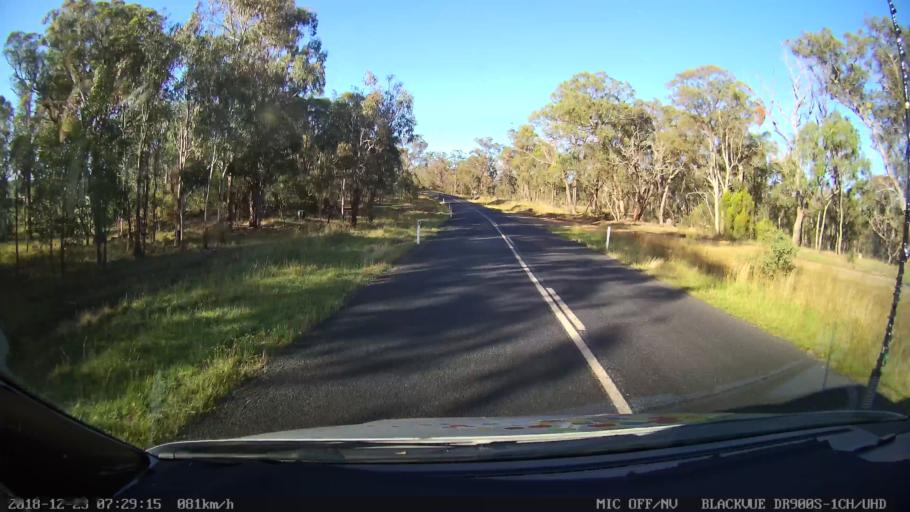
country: AU
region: New South Wales
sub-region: Armidale Dumaresq
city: Enmore
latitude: -30.4933
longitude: 152.1579
